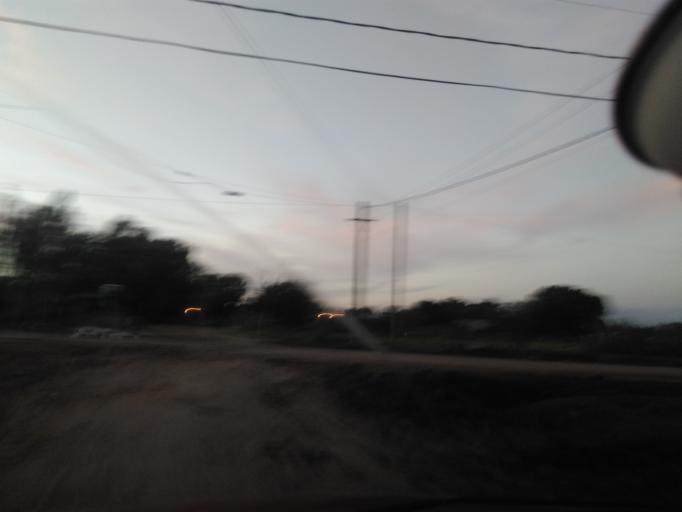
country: AR
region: Chaco
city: Resistencia
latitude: -27.4456
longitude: -58.9663
